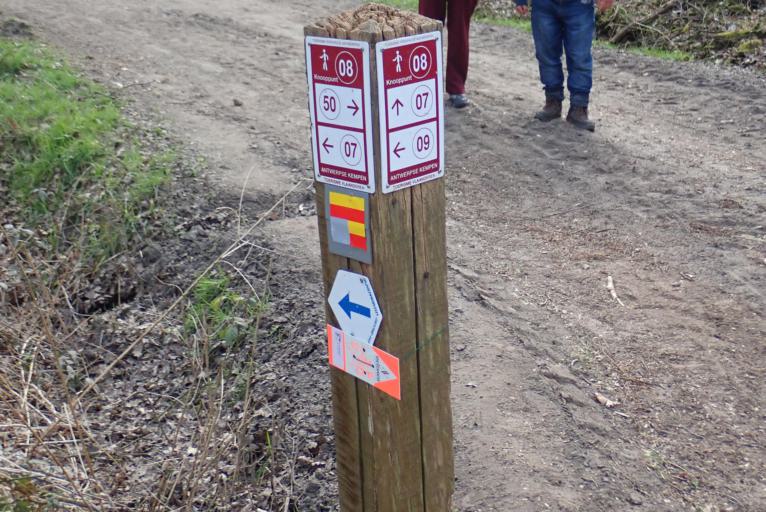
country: BE
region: Flanders
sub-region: Provincie Antwerpen
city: Brecht
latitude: 51.3284
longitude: 4.6565
